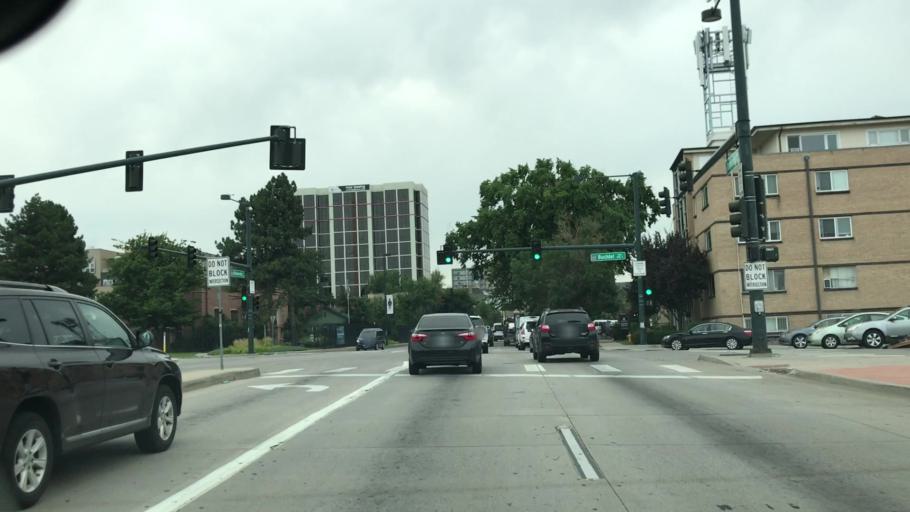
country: US
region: Colorado
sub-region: Arapahoe County
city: Glendale
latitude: 39.6832
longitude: -104.9595
